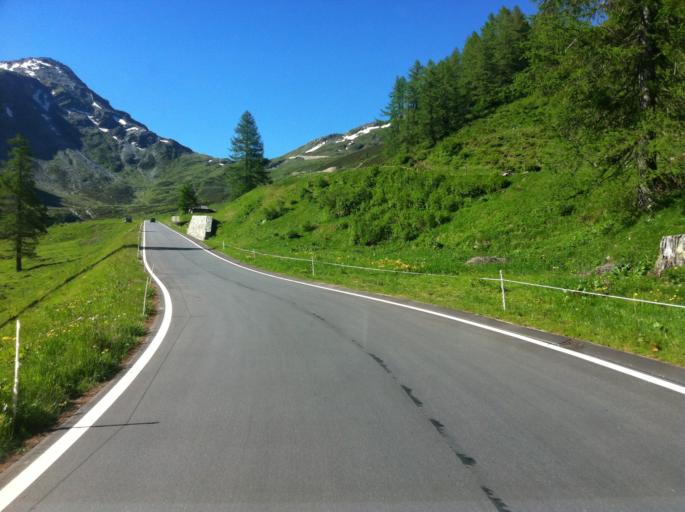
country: CH
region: Grisons
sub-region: Hinterrhein District
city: Hinterrhein
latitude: 46.5335
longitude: 9.3267
